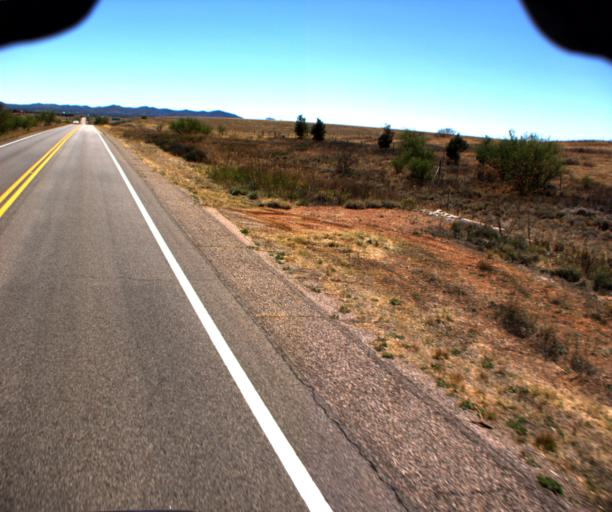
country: US
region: Arizona
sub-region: Pima County
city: Corona de Tucson
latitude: 31.7140
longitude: -110.6555
